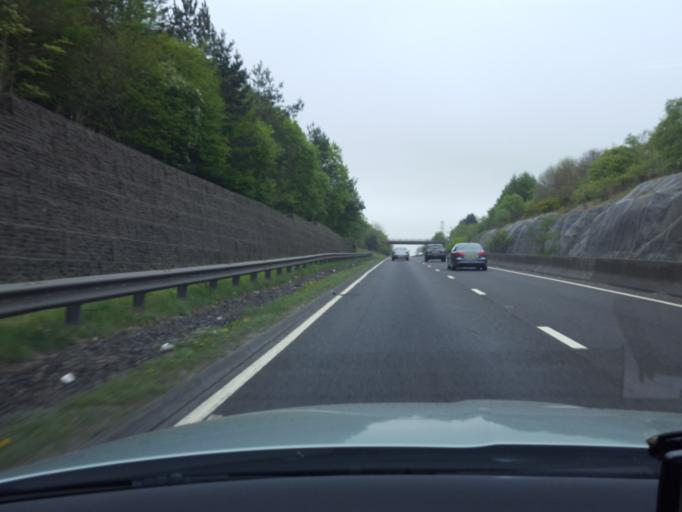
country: GB
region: Scotland
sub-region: Dundee City
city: Dundee
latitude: 56.5012
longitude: -2.9488
